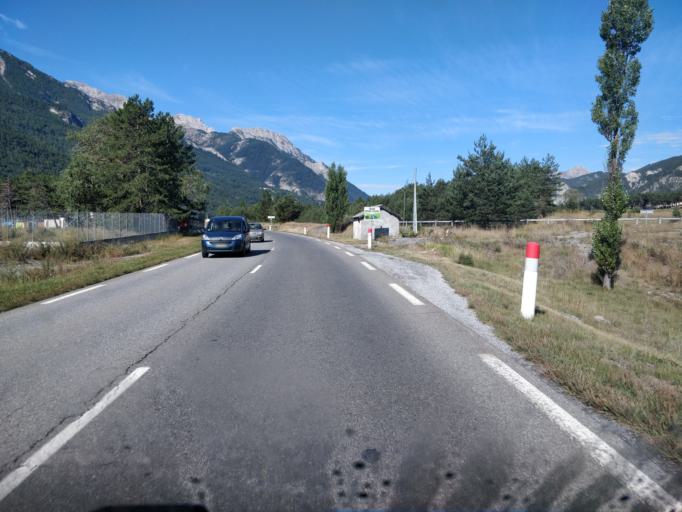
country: FR
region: Provence-Alpes-Cote d'Azur
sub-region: Departement des Alpes-de-Haute-Provence
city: Barcelonnette
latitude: 44.3863
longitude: 6.6157
